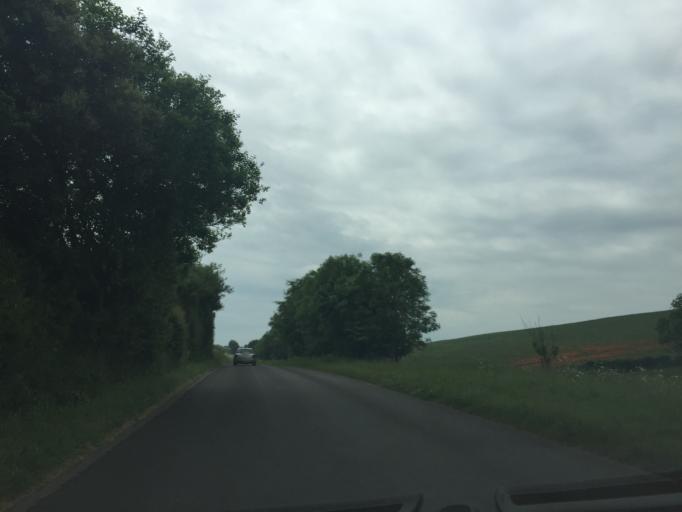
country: GB
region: England
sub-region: Dorset
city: Wool
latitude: 50.6423
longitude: -2.2669
